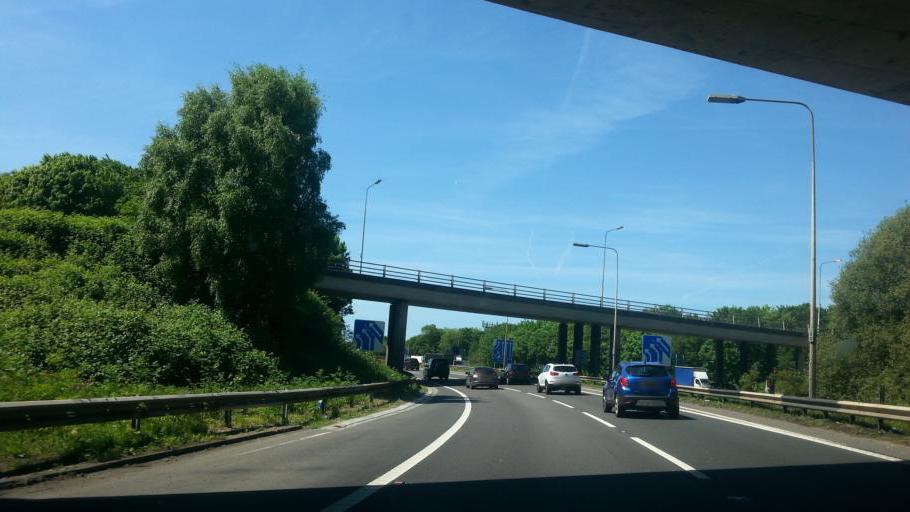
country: GB
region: England
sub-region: Surrey
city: Virginia Water
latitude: 51.3999
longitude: -0.5392
